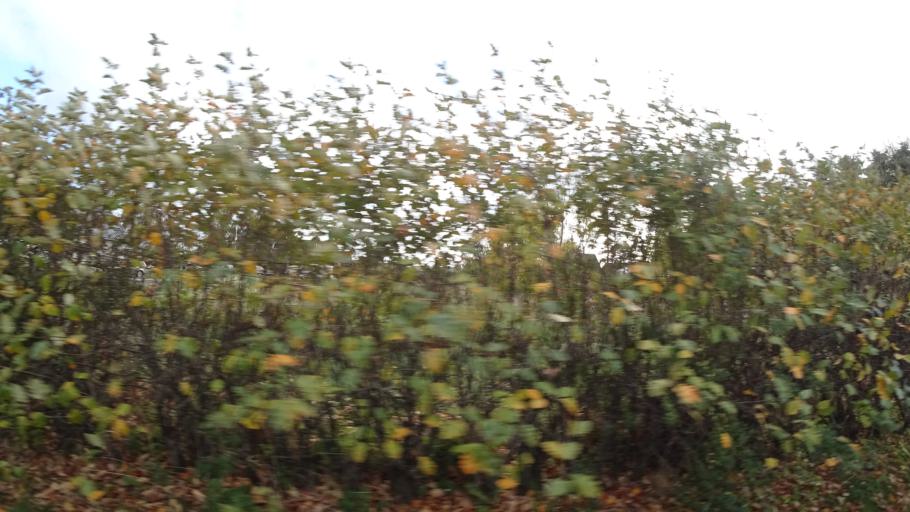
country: SE
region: Skane
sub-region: Staffanstorps Kommun
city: Staffanstorp
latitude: 55.6274
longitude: 13.2262
